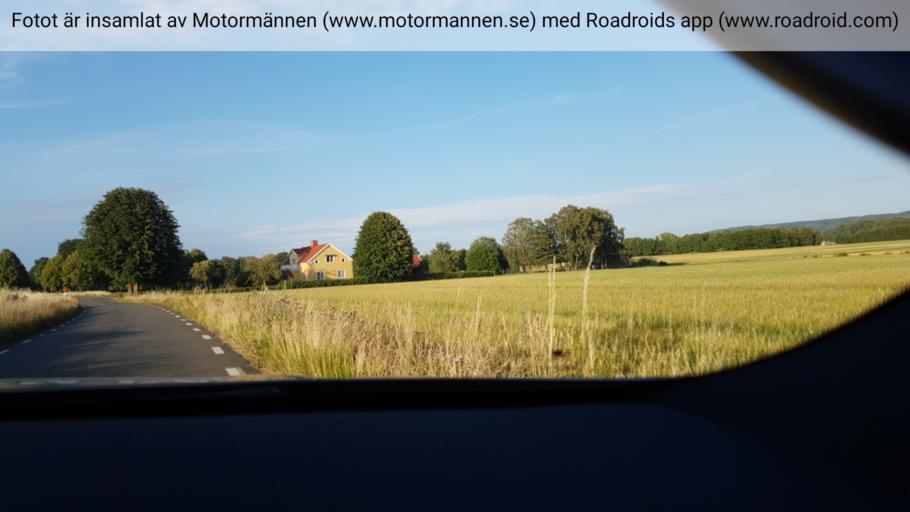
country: SE
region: Vaestra Goetaland
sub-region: Skara Kommun
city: Axvall
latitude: 58.3776
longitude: 13.5727
